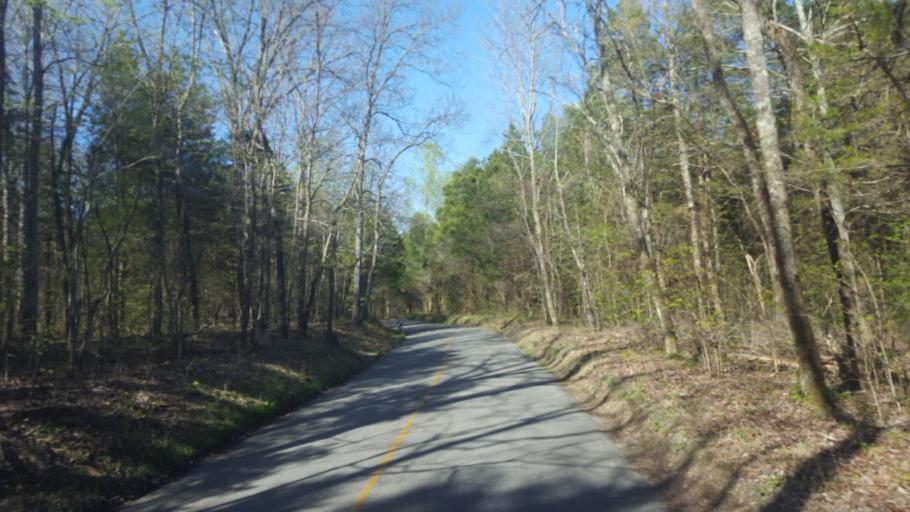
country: US
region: Kentucky
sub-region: Barren County
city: Cave City
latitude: 37.1584
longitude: -86.0462
